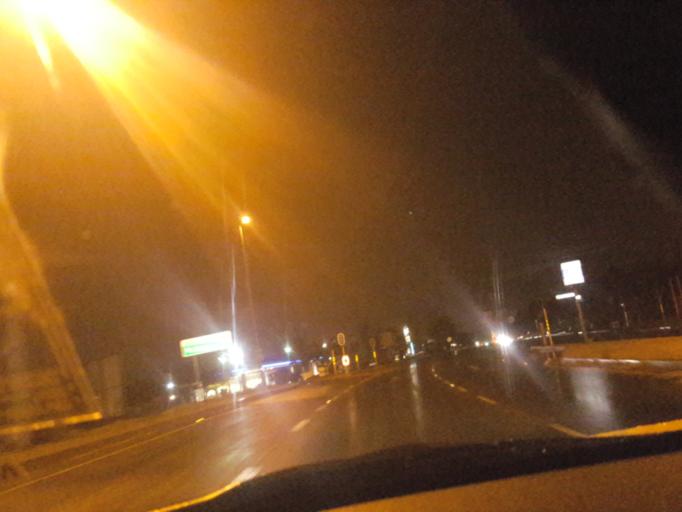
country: ZA
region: Gauteng
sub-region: City of Johannesburg Metropolitan Municipality
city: Diepsloot
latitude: -25.9872
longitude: 27.9846
